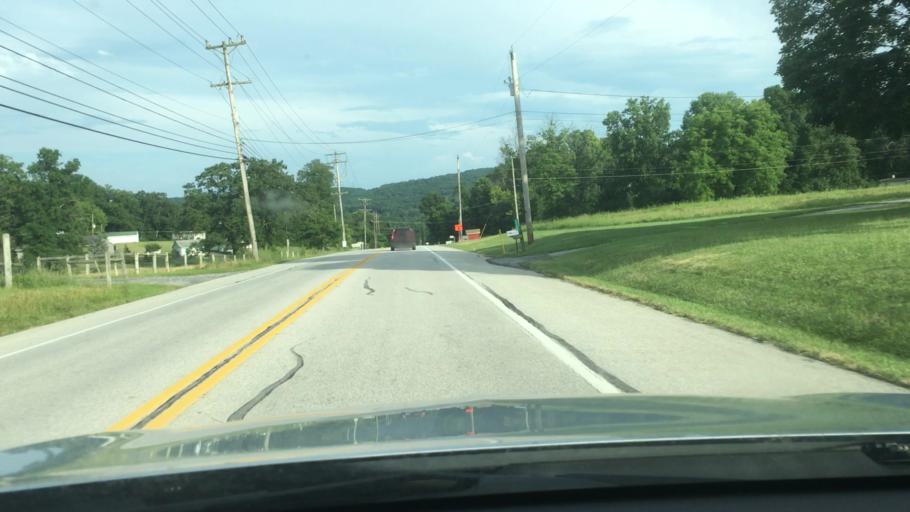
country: US
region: Pennsylvania
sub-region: York County
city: Dover
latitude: 40.0500
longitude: -76.9051
